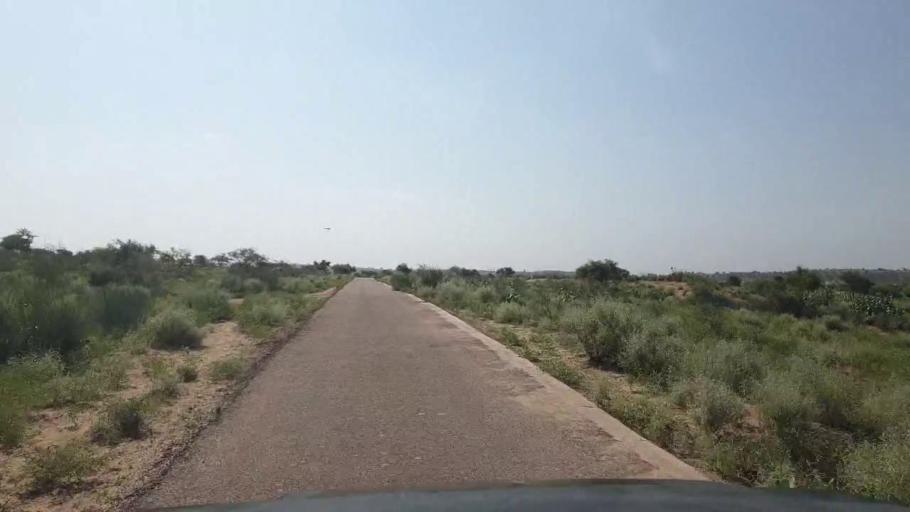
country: PK
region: Sindh
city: Islamkot
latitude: 25.1753
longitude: 70.3967
